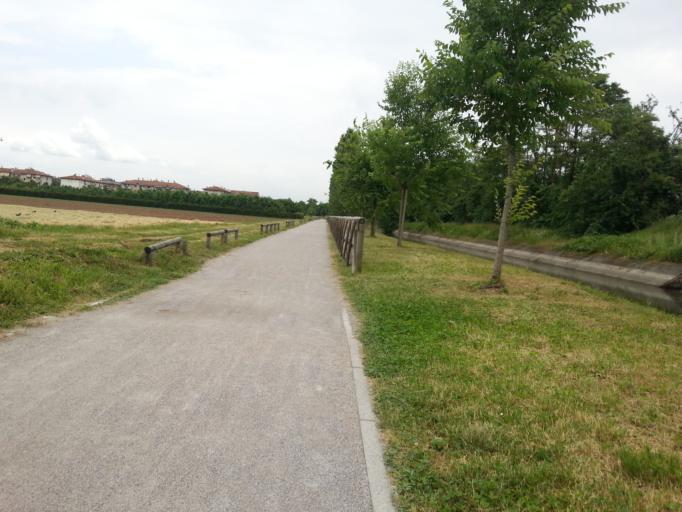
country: IT
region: Lombardy
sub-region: Provincia di Monza e Brianza
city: Nova Milanese
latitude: 45.5879
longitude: 9.1825
